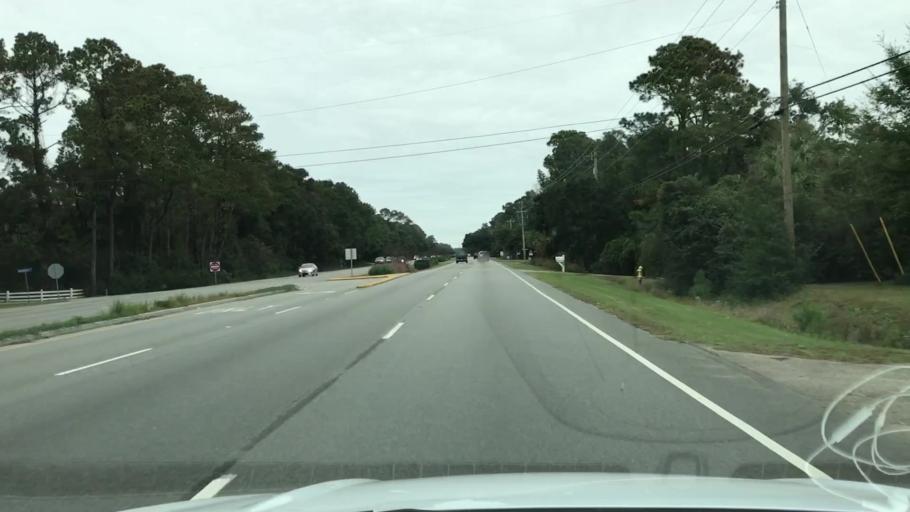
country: US
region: South Carolina
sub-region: Georgetown County
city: Murrells Inlet
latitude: 33.4608
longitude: -79.1119
